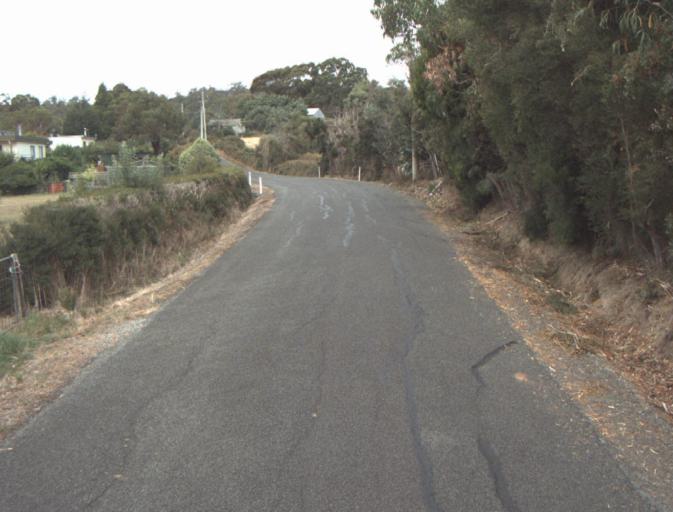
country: AU
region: Tasmania
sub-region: Launceston
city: Mayfield
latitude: -41.2935
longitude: 147.0234
